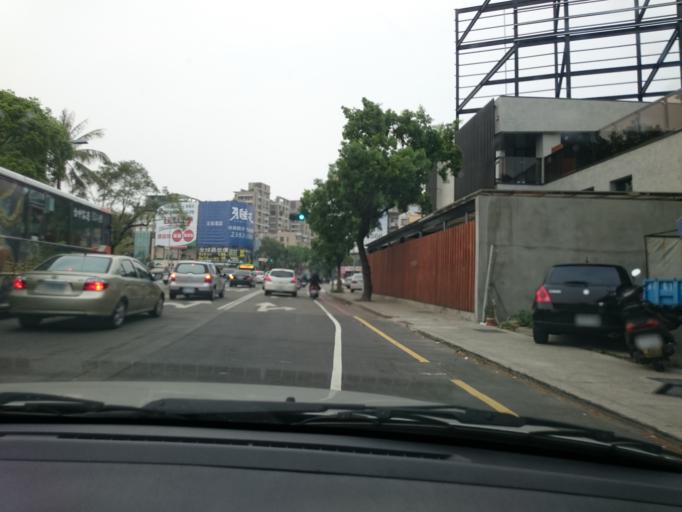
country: TW
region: Taiwan
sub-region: Taichung City
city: Taichung
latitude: 24.1608
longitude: 120.6339
